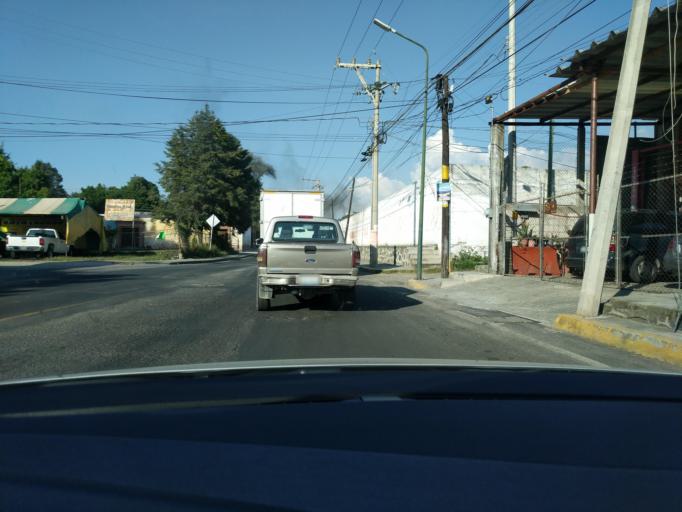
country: MX
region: Puebla
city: San Andres Cholula
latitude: 19.0326
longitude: -98.3184
